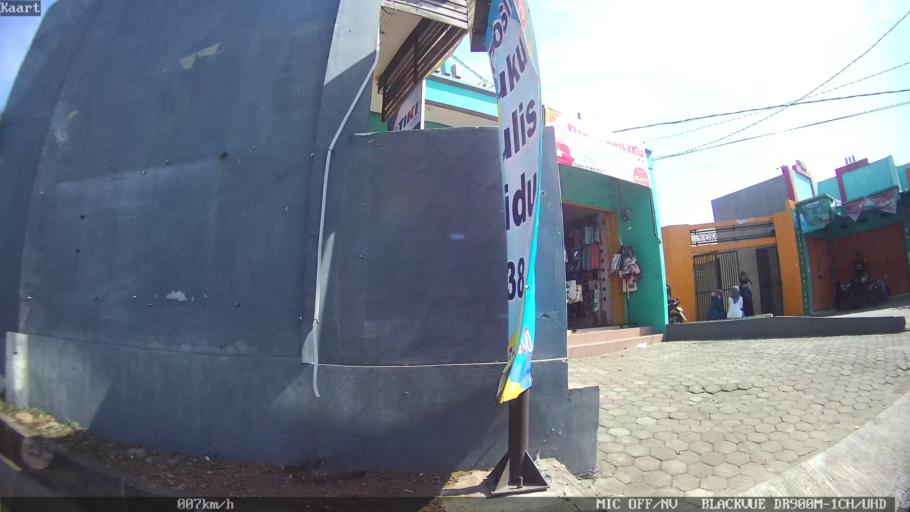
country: ID
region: Lampung
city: Kedaton
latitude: -5.3642
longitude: 105.2472
